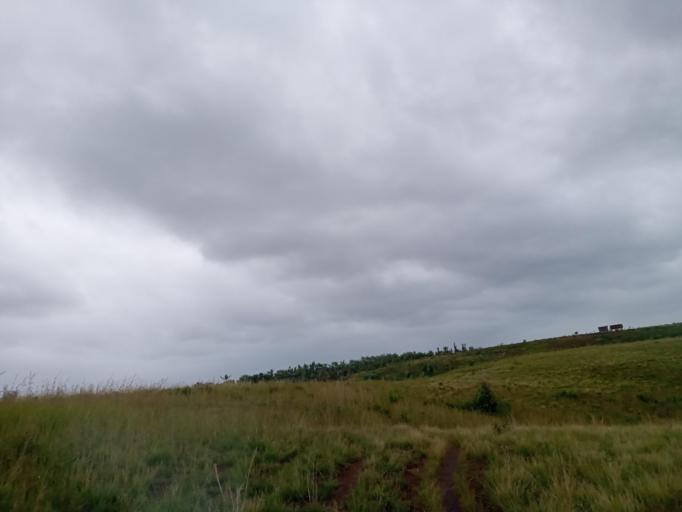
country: MG
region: Atsimo-Atsinanana
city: Vohipaho
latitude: -23.9083
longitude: 47.5175
